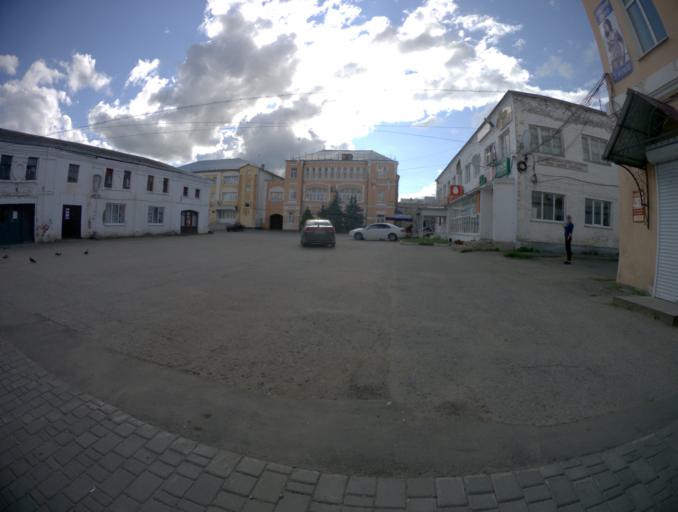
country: RU
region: Vladimir
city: Yur'yev-Pol'skiy
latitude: 56.5004
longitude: 39.6814
